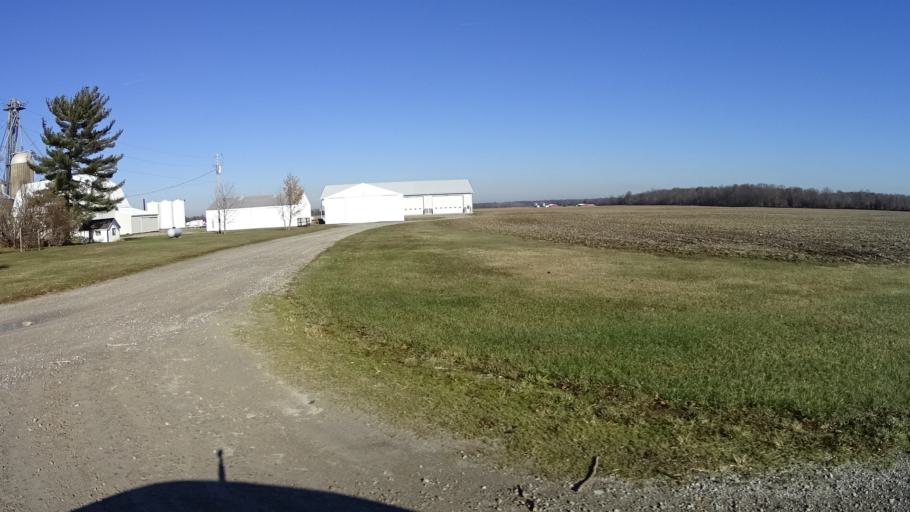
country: US
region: Ohio
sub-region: Huron County
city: New London
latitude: 41.0738
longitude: -82.2989
